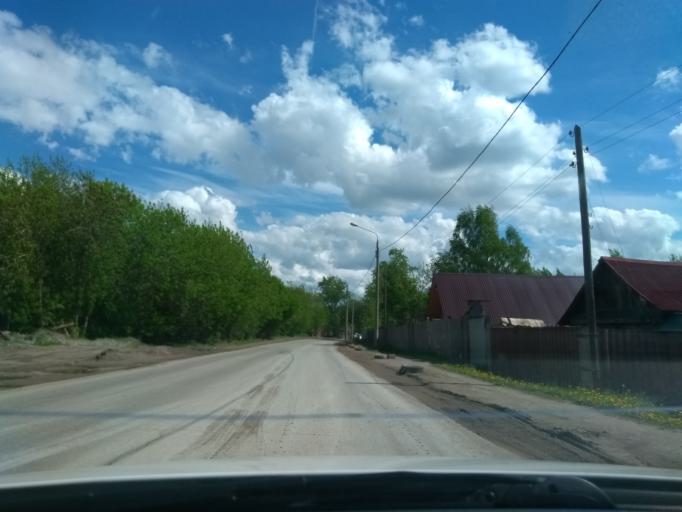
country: RU
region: Perm
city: Kondratovo
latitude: 58.0069
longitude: 56.1155
